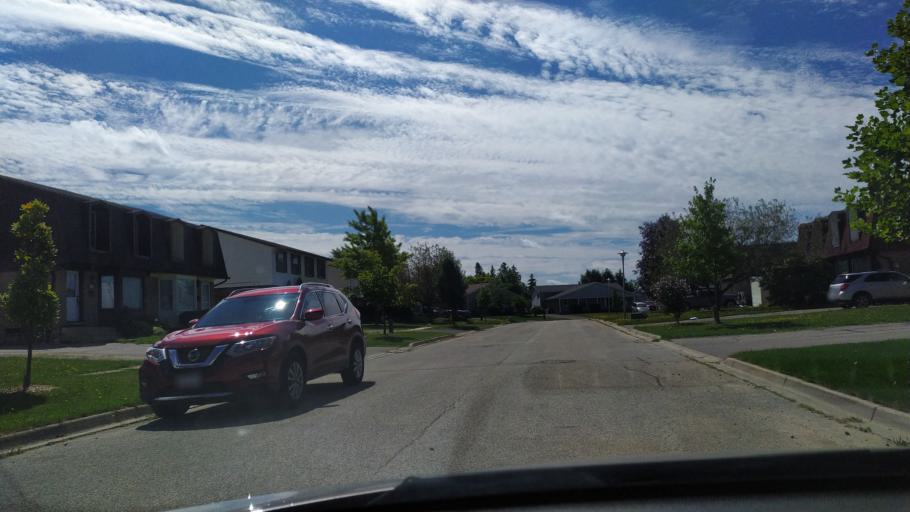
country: CA
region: Ontario
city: Stratford
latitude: 43.3732
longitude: -80.9436
